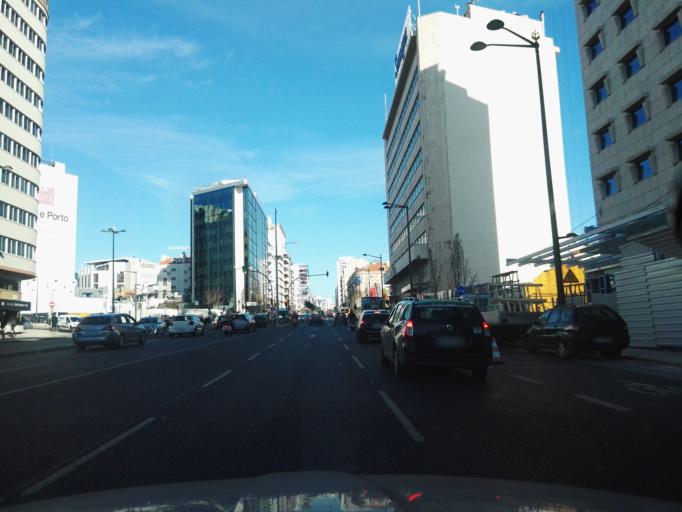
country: PT
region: Lisbon
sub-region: Lisbon
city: Lisbon
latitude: 38.7274
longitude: -9.1487
